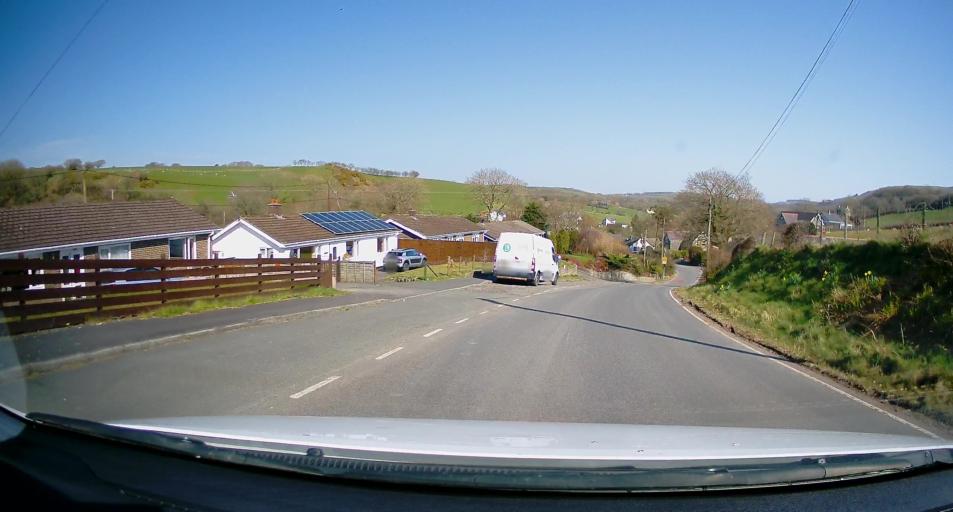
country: GB
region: Wales
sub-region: County of Ceredigion
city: Lledrod
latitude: 52.3151
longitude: -4.0585
